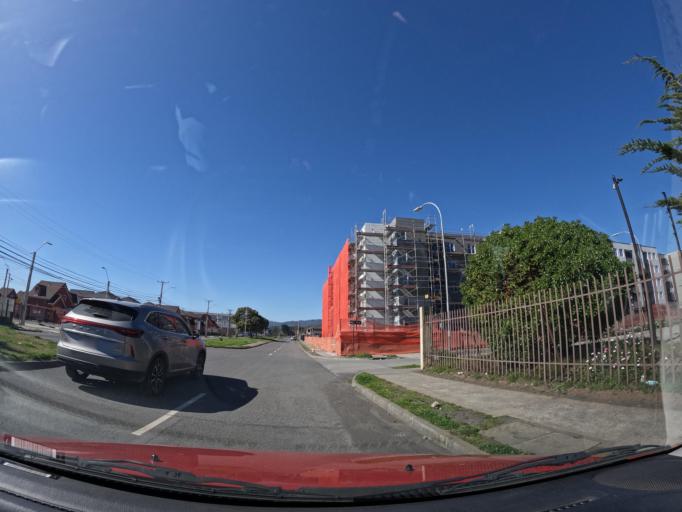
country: CL
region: Biobio
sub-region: Provincia de Concepcion
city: Concepcion
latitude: -36.8824
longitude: -73.1477
